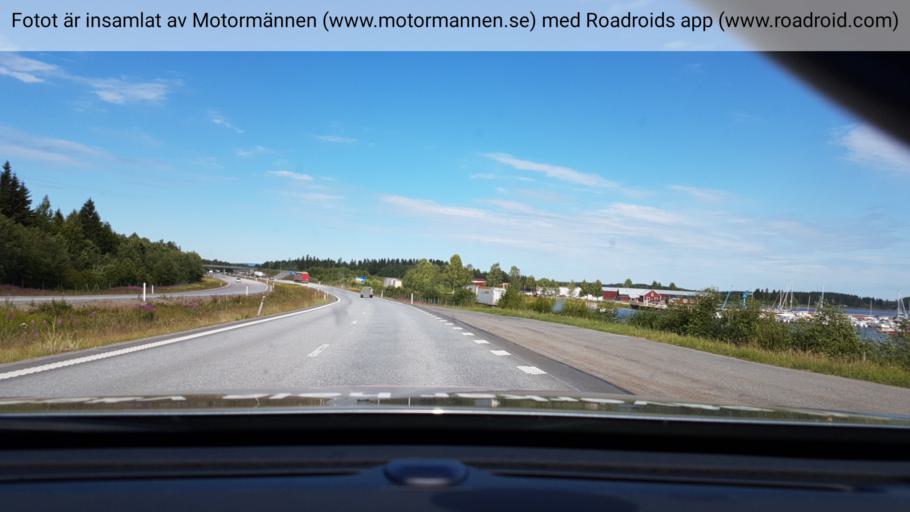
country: SE
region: Vaesterbotten
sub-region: Skelleftea Kommun
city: Kage
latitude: 64.8243
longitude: 21.0250
